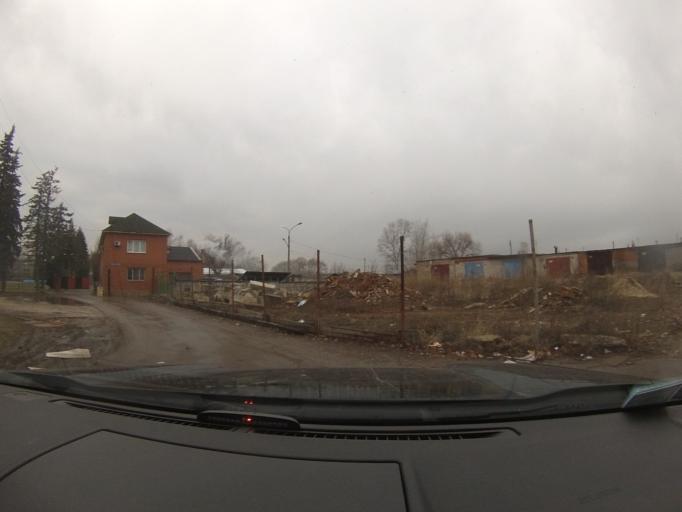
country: RU
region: Moskovskaya
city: Lopatinskiy
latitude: 55.3442
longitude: 38.7273
